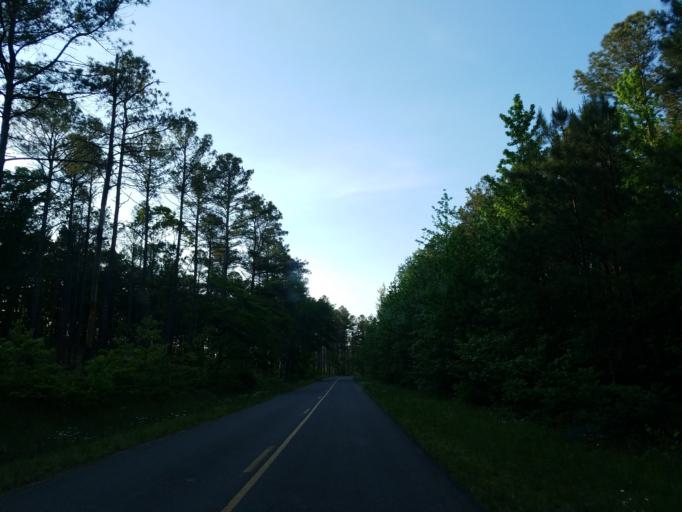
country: US
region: Georgia
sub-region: Whitfield County
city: Dalton
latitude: 34.6318
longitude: -85.0804
